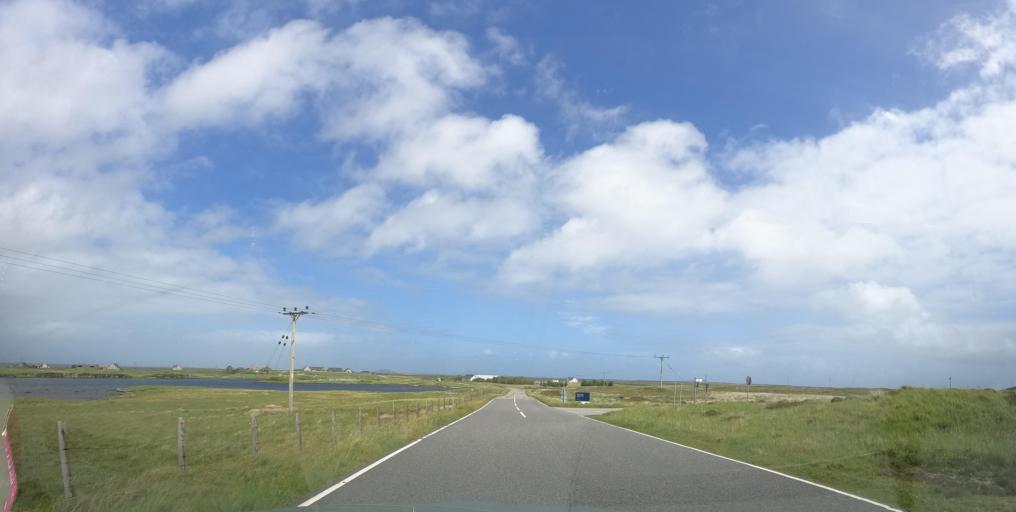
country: GB
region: Scotland
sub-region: Eilean Siar
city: Benbecula
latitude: 57.3476
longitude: -7.3597
